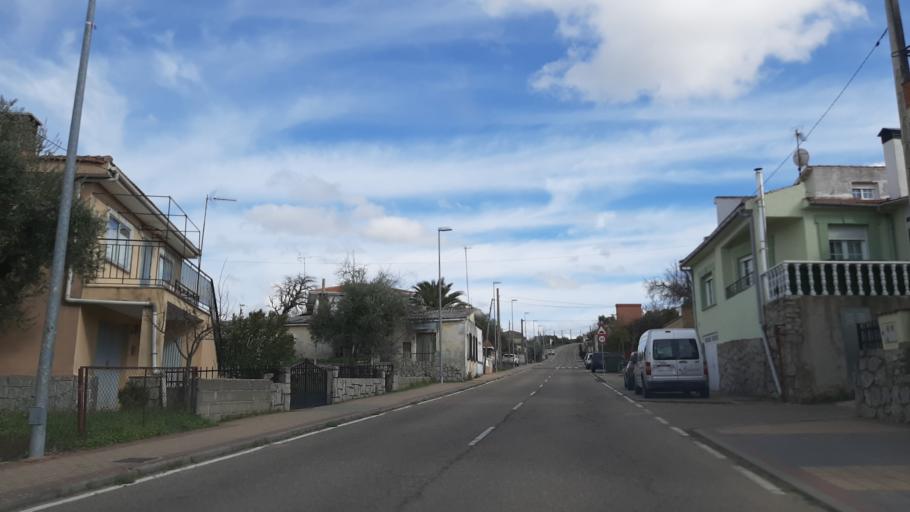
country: ES
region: Castille and Leon
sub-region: Provincia de Salamanca
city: Villarino de los Aires
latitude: 41.2687
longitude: -6.4633
